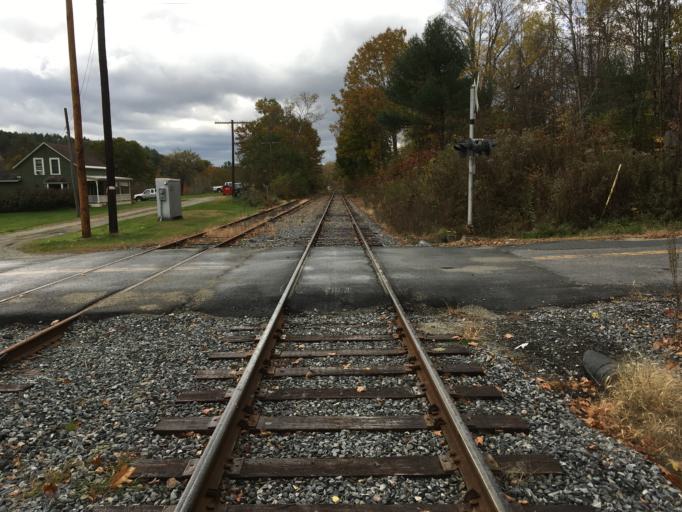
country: US
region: New Hampshire
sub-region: Grafton County
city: Woodsville
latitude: 44.2054
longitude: -72.0606
